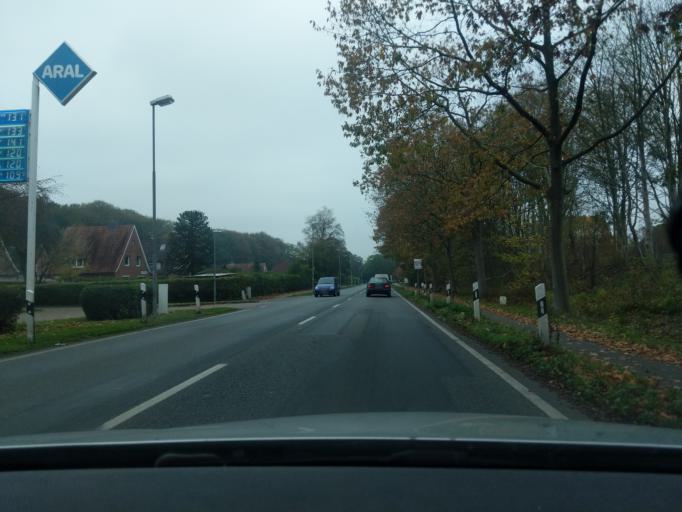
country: DE
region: Lower Saxony
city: Himmelpforten
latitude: 53.6101
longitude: 9.3144
